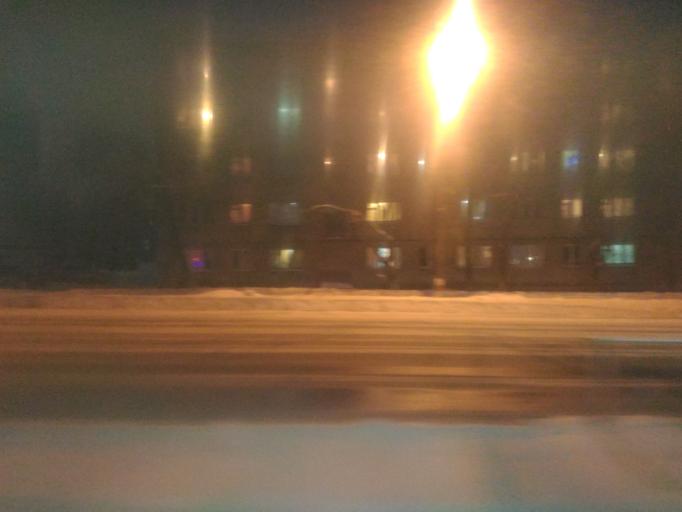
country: RU
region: Ulyanovsk
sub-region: Ulyanovskiy Rayon
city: Ulyanovsk
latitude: 54.3460
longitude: 48.3724
